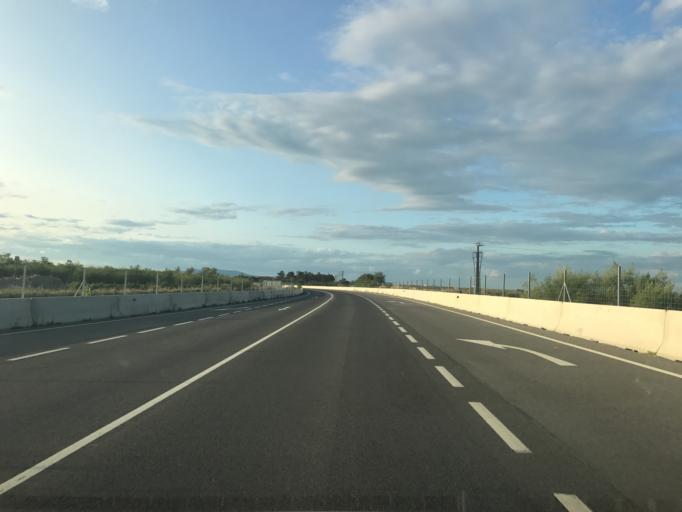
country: AT
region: Lower Austria
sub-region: Politischer Bezirk Wiener Neustadt
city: Lichtenworth
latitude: 47.8606
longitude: 16.2729
